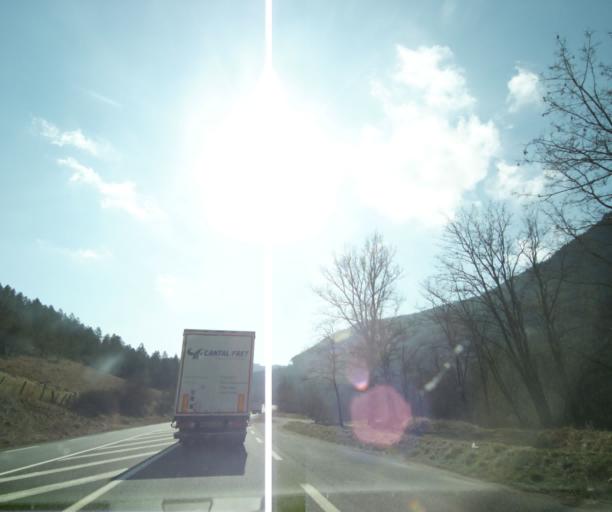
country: FR
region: Languedoc-Roussillon
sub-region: Departement de la Lozere
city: Chanac
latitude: 44.4906
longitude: 3.4184
